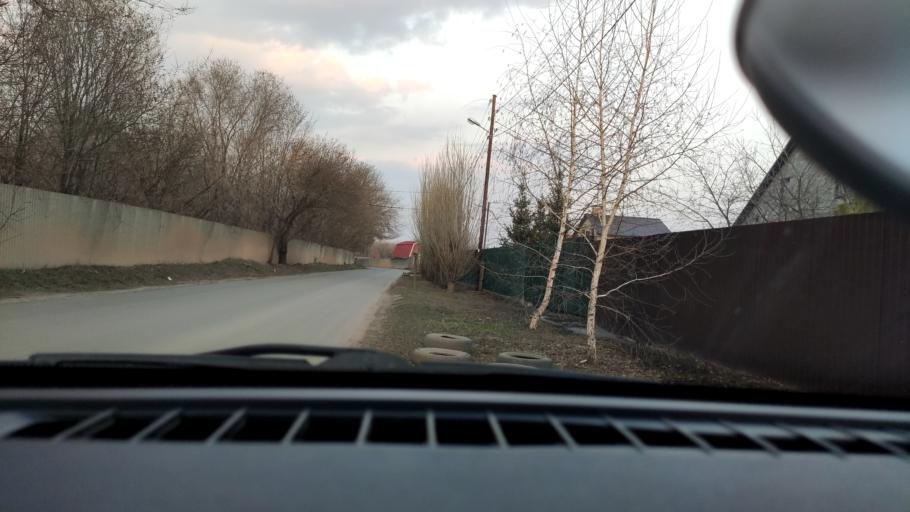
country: RU
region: Samara
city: Smyshlyayevka
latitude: 53.2082
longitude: 50.3237
